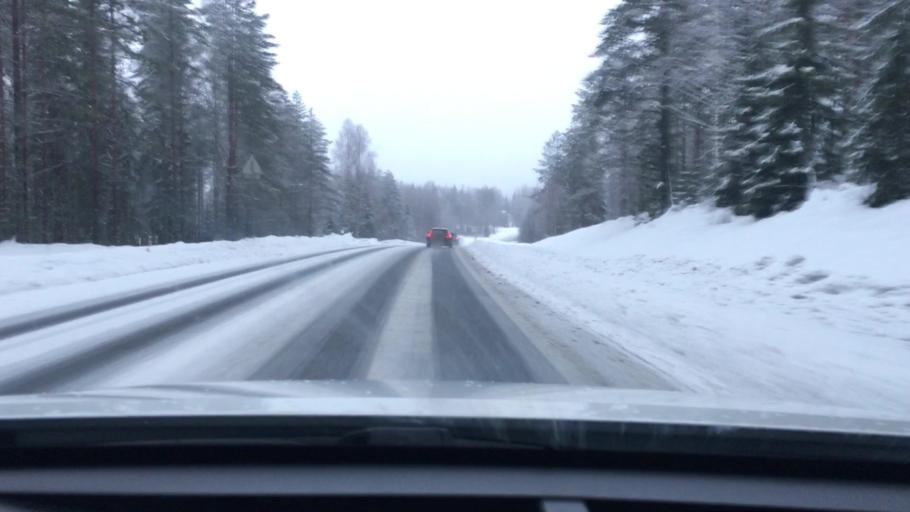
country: FI
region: Northern Savo
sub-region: Ylae-Savo
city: Sonkajaervi
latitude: 63.7651
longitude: 27.4110
